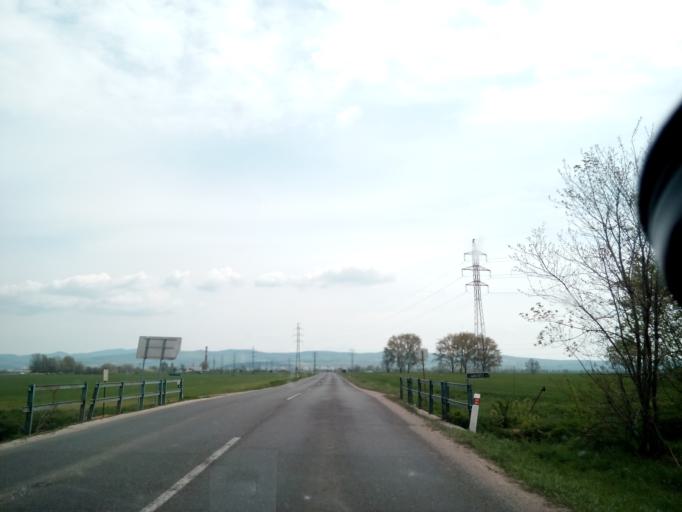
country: SK
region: Trnavsky
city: Vrbove
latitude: 48.5890
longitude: 17.7609
